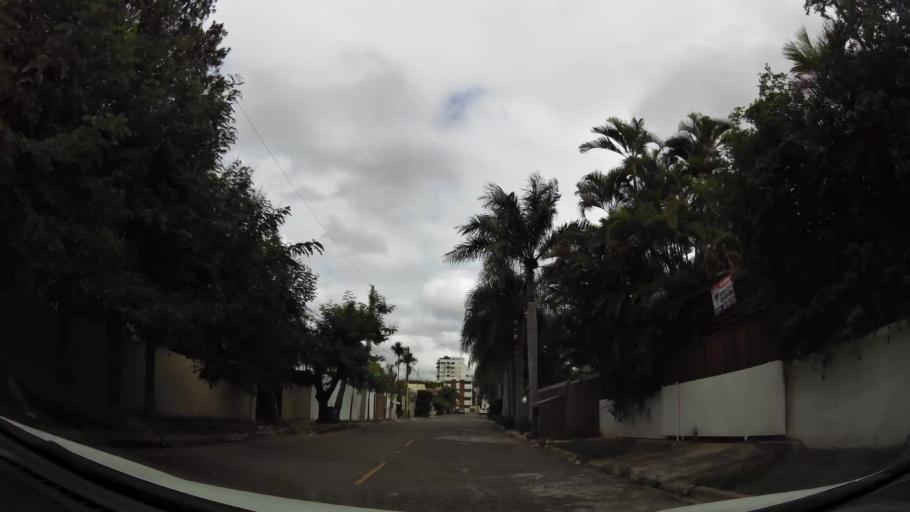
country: DO
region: Nacional
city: Bella Vista
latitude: 18.4499
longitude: -69.9447
